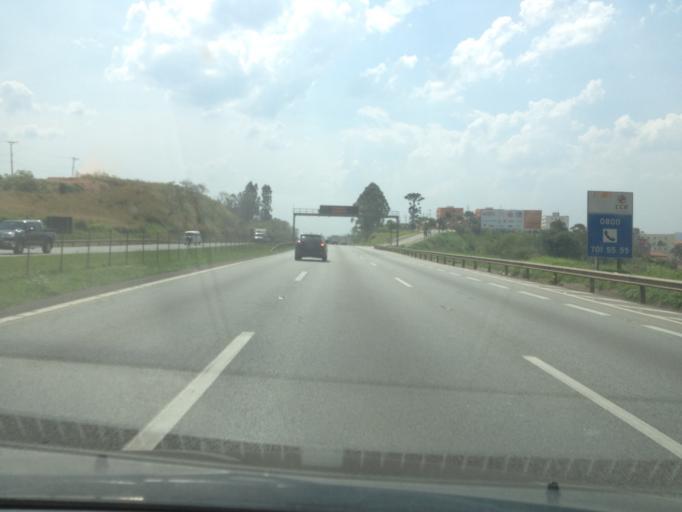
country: BR
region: Sao Paulo
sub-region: Pirapora Do Bom Jesus
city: Pirapora do Bom Jesus
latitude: -23.4459
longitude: -47.0603
